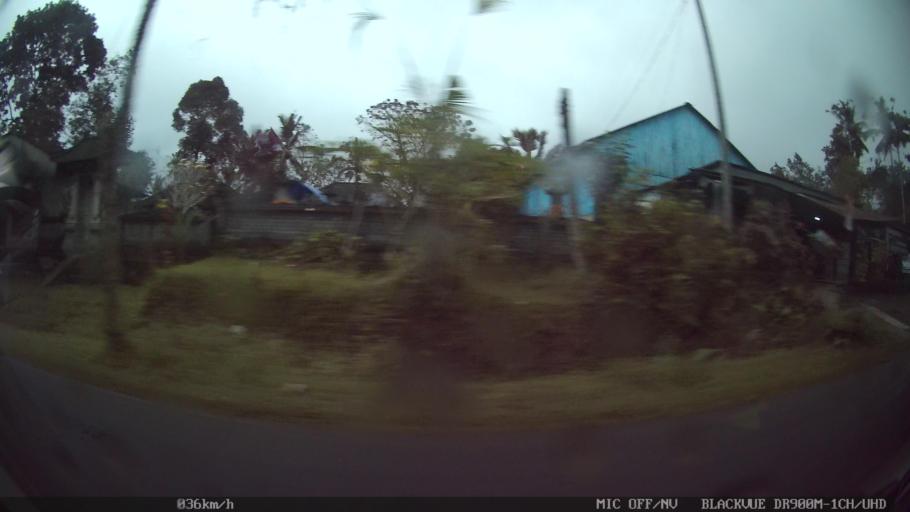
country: ID
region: Bali
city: Banjar Ponggang
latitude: -8.3915
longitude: 115.2574
